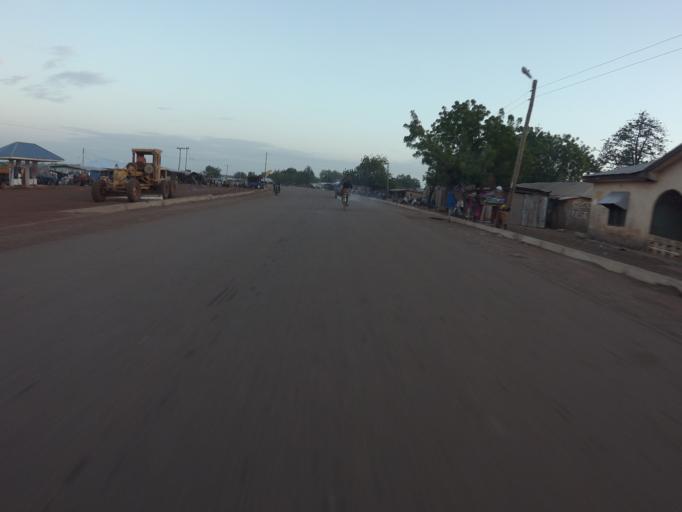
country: GH
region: Northern
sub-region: Yendi
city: Yendi
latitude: 9.9200
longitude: -0.2163
